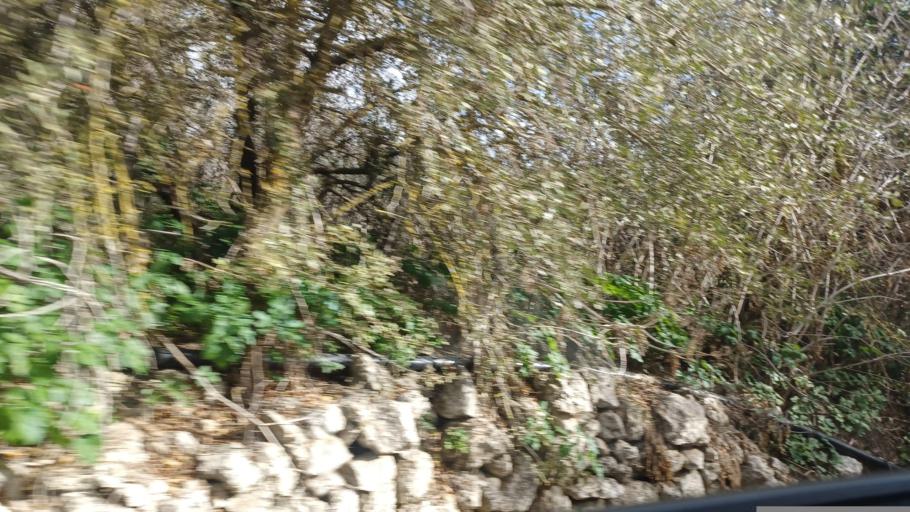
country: CY
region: Pafos
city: Mesogi
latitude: 34.8827
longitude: 32.5107
